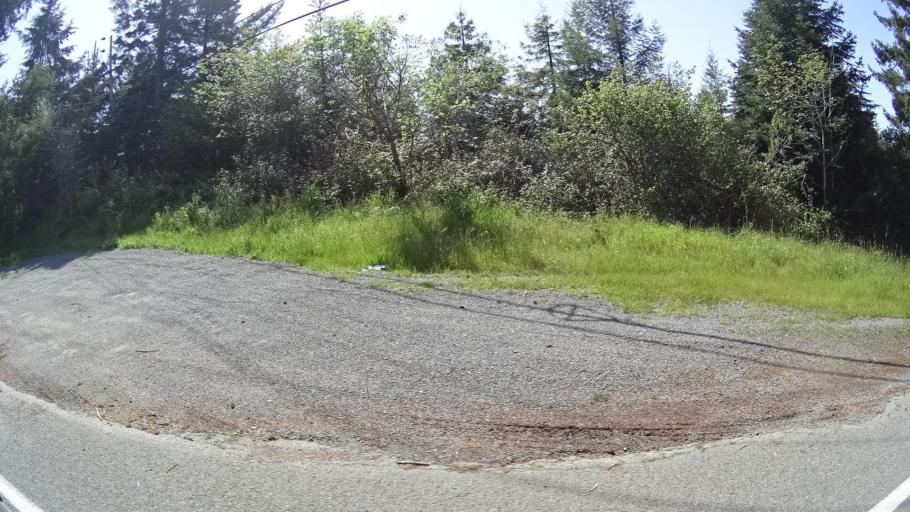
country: US
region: California
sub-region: Humboldt County
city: Hydesville
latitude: 40.5502
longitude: -124.1057
